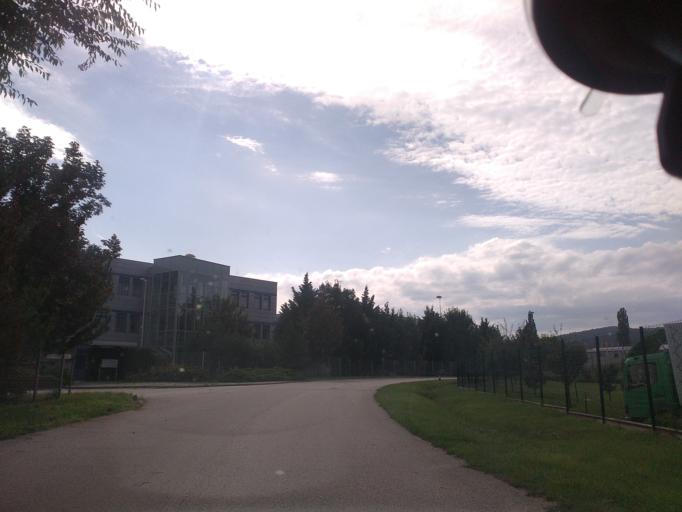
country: HU
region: Komarom-Esztergom
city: Piliscsev
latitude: 47.6757
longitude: 18.7876
